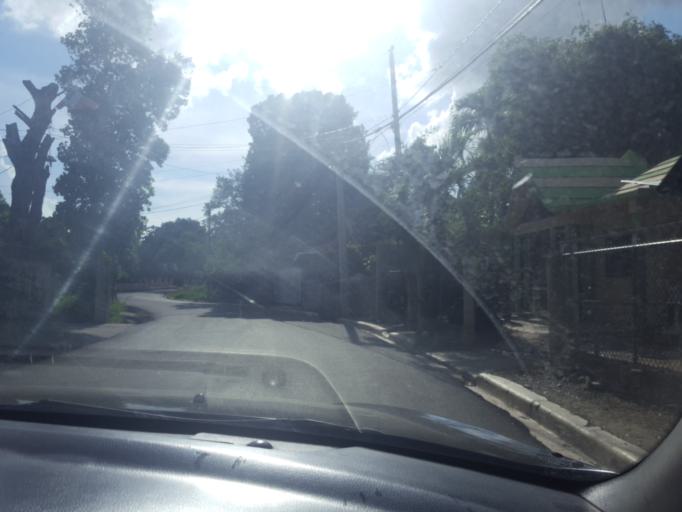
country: DO
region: Santiago
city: Licey al Medio
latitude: 19.3721
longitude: -70.6274
